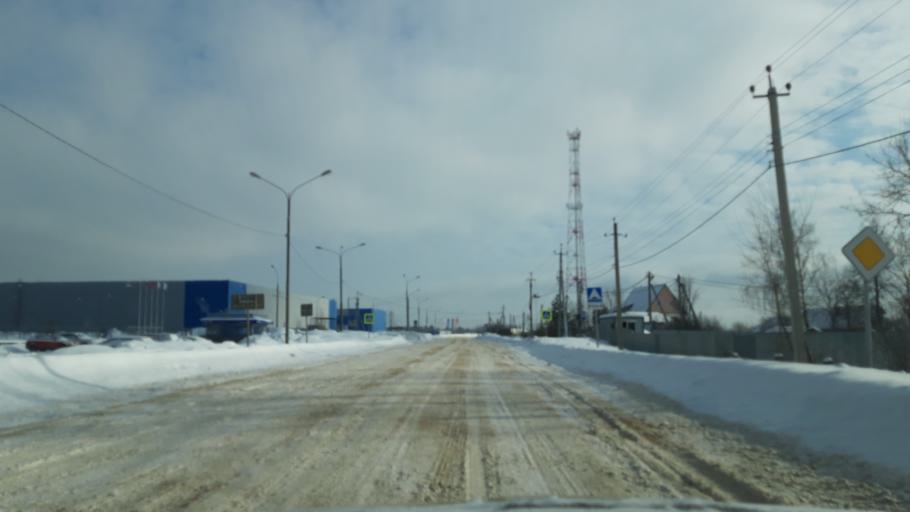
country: RU
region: Moskovskaya
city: Yermolino
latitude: 56.1438
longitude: 37.3757
